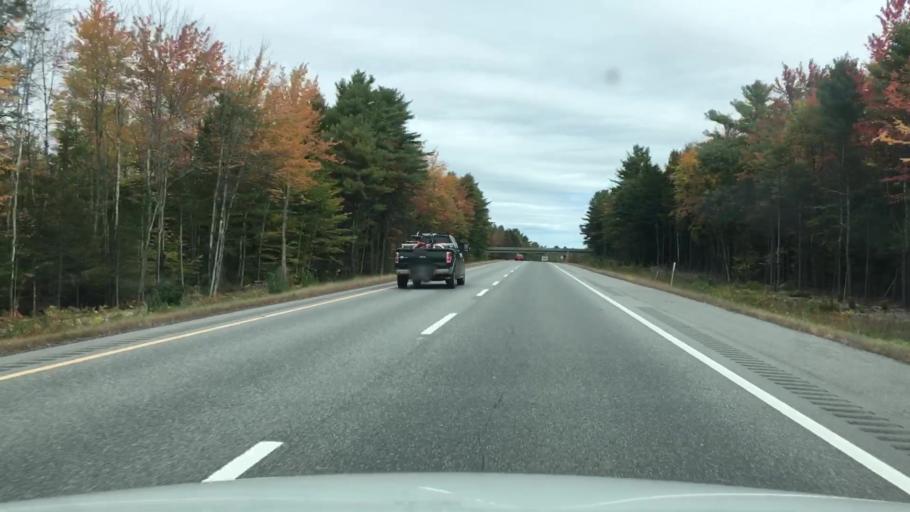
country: US
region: Maine
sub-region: Kennebec County
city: Sidney
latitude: 44.4195
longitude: -69.7419
